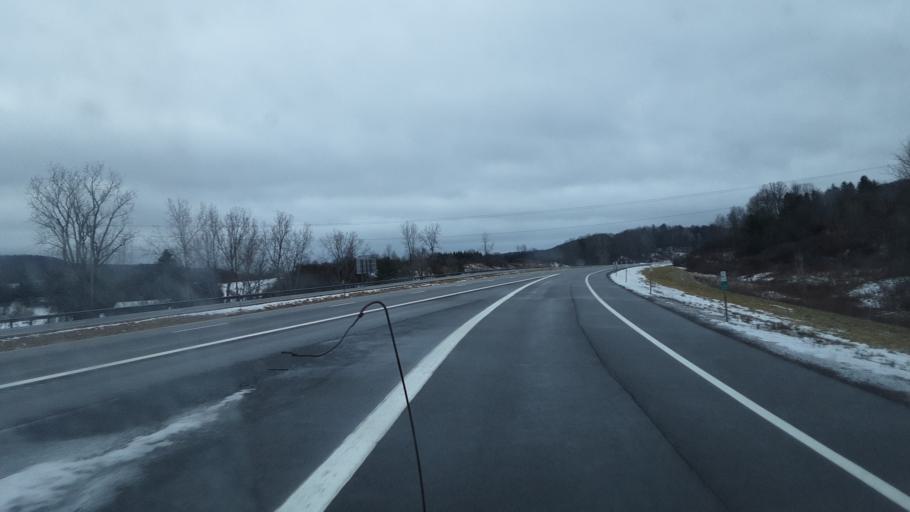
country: US
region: New York
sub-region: Allegany County
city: Alfred
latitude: 42.3220
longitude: -77.7442
